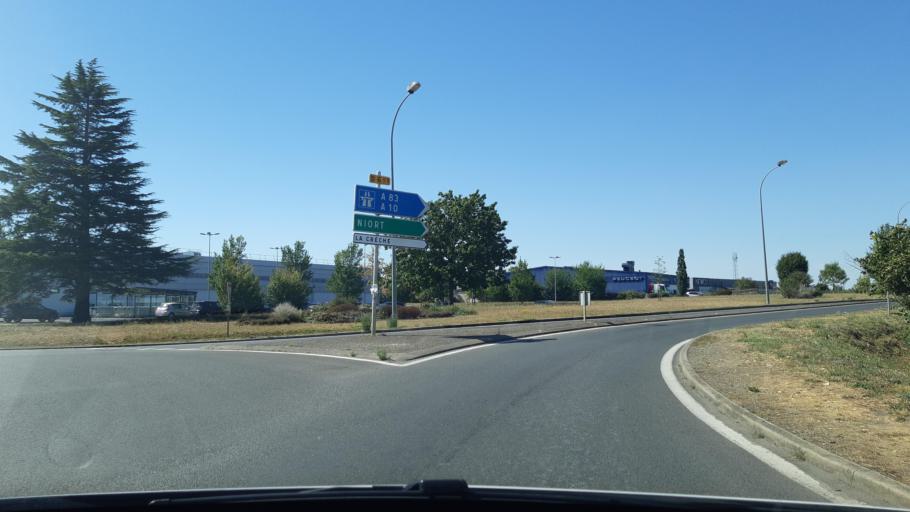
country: FR
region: Poitou-Charentes
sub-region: Departement des Deux-Sevres
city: Azay-le-Brule
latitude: 46.4074
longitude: -0.2230
